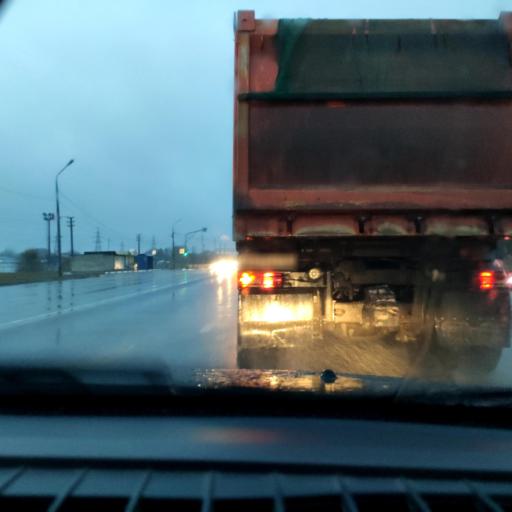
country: RU
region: Samara
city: Tol'yatti
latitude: 53.5618
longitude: 49.2896
